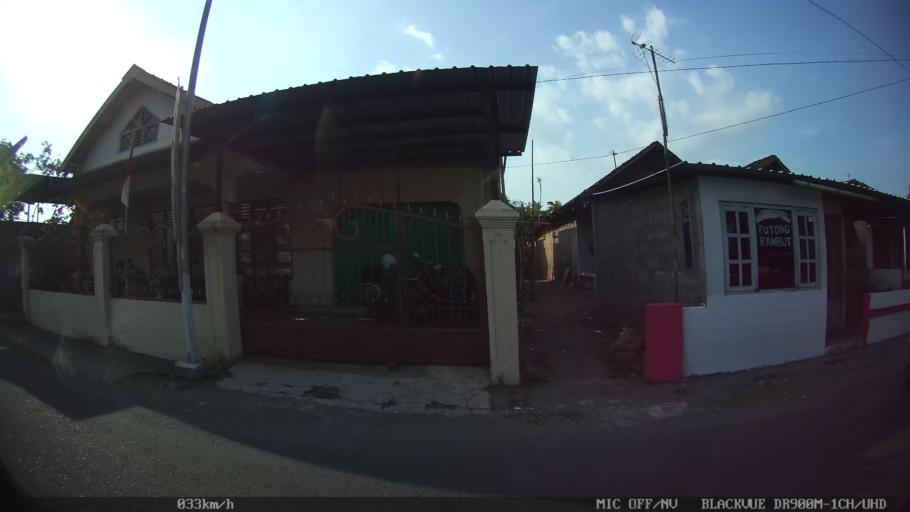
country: ID
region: Daerah Istimewa Yogyakarta
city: Bantul
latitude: -7.8907
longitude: 110.3224
